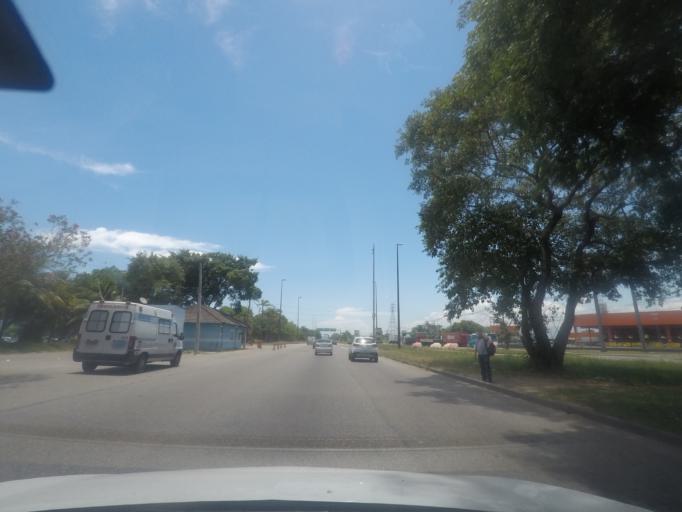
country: BR
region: Rio de Janeiro
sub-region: Itaguai
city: Itaguai
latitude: -22.8936
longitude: -43.6756
